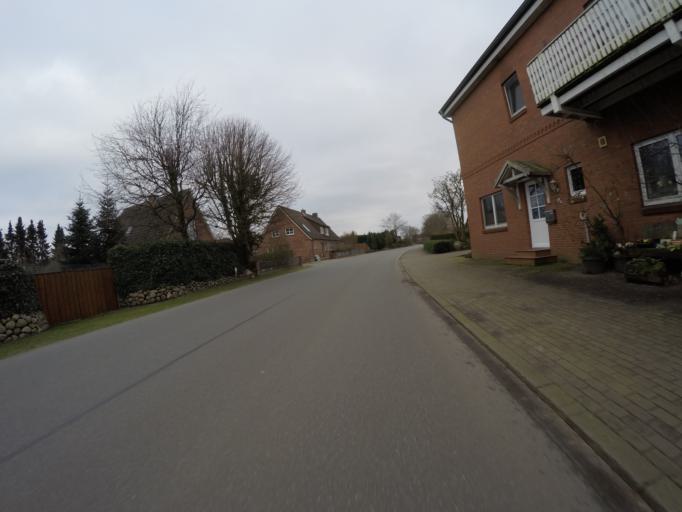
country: DE
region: Schleswig-Holstein
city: Langeln
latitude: 53.7953
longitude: 9.8558
